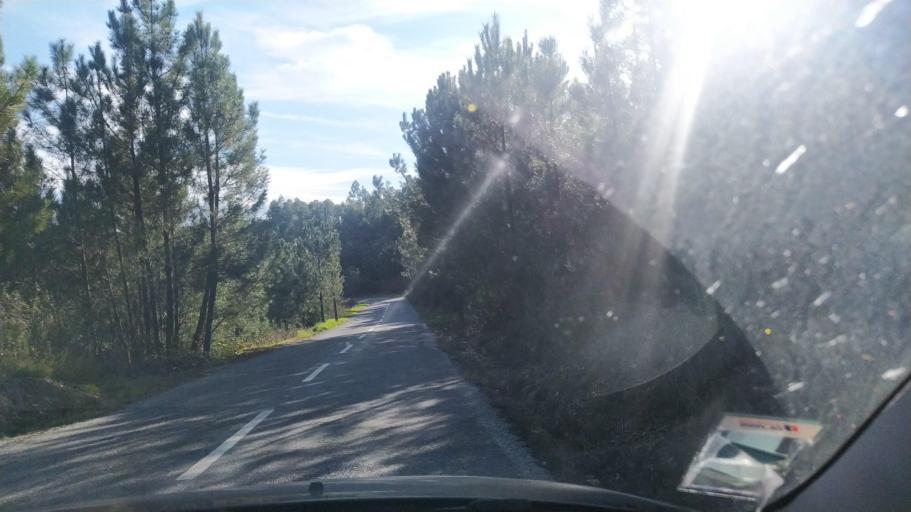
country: PT
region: Castelo Branco
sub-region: Concelho do Fundao
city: Aldeia de Joanes
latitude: 40.1856
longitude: -7.7012
